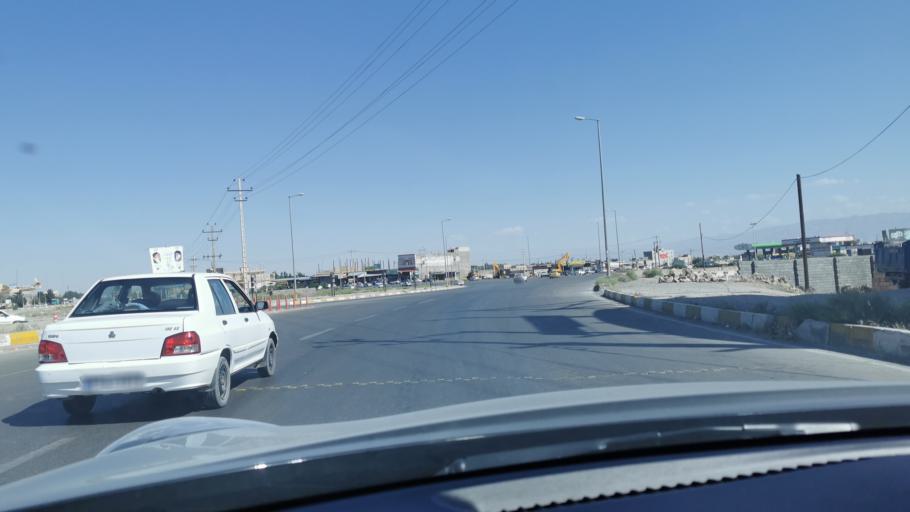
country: IR
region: Razavi Khorasan
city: Chenaran
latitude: 36.6329
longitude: 59.1330
